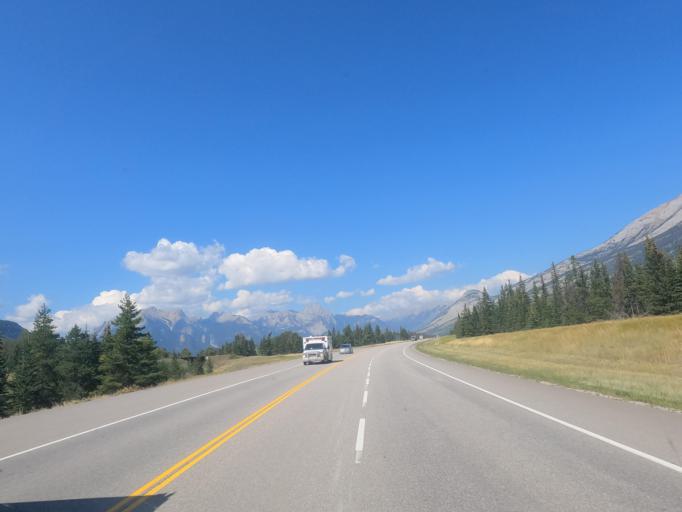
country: CA
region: Alberta
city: Jasper Park Lodge
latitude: 52.9697
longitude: -118.0567
